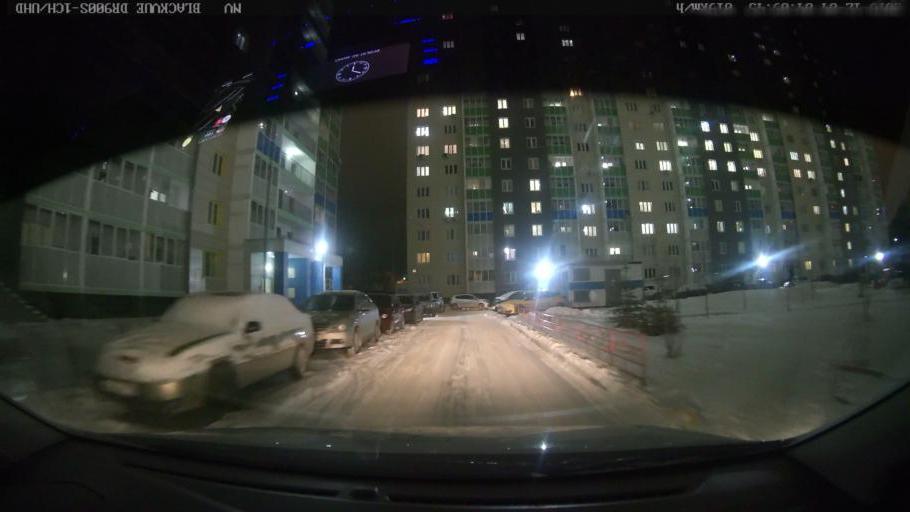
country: RU
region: Tatarstan
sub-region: Gorod Kazan'
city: Kazan
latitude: 55.8032
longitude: 49.2391
